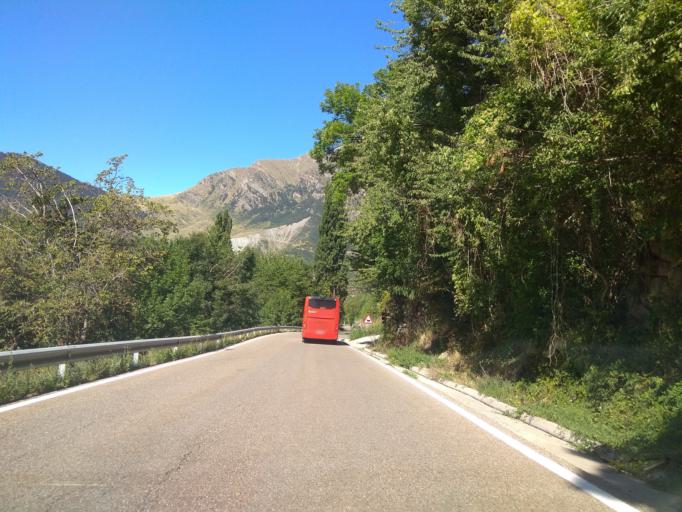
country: ES
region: Catalonia
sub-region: Provincia de Lleida
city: Vielha
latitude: 42.5197
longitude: 0.8459
